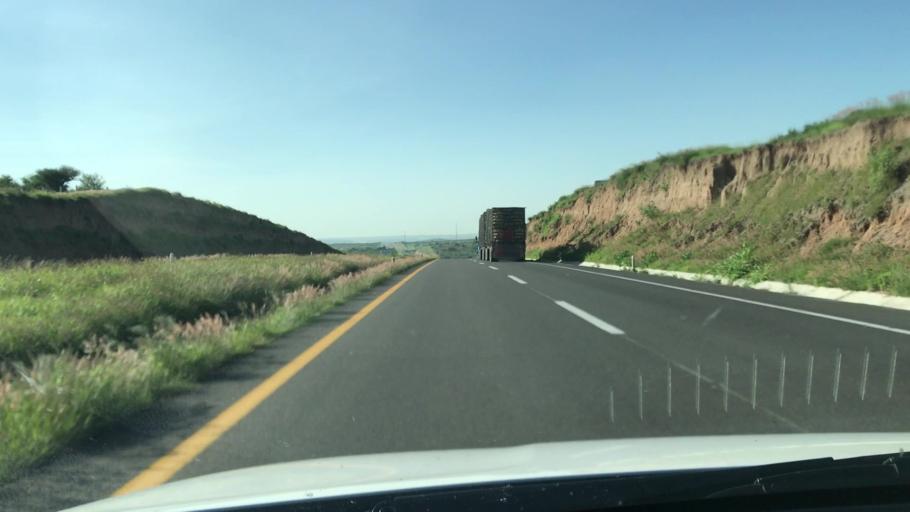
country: MX
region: Jalisco
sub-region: Union de San Antonio
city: San Jose del Caliche (El Caliche)
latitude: 21.2067
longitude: -101.9071
